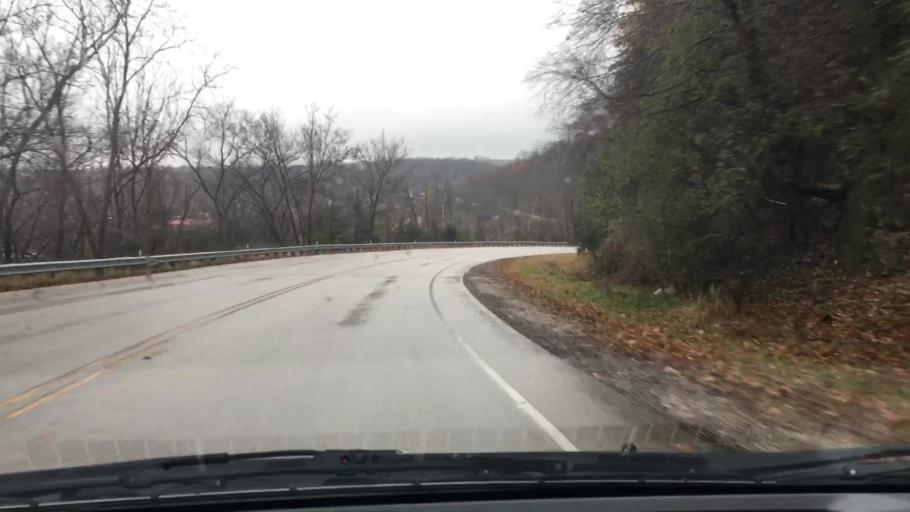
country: US
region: Minnesota
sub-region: Fillmore County
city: Preston
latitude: 43.7250
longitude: -91.9799
